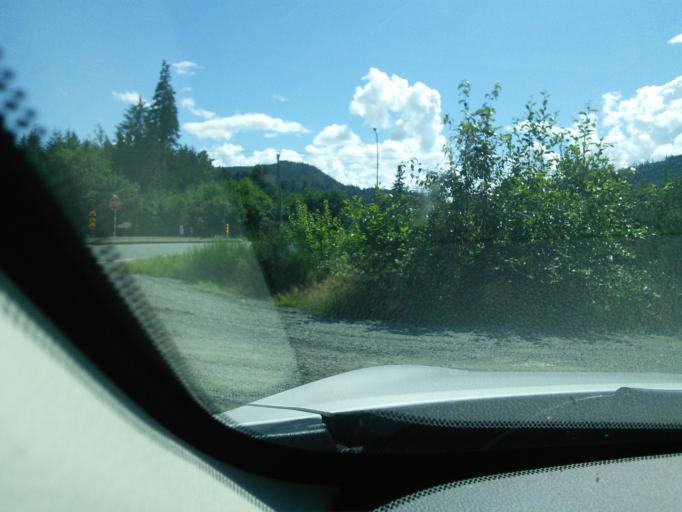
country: CA
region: British Columbia
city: Campbell River
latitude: 50.3123
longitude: -125.9192
